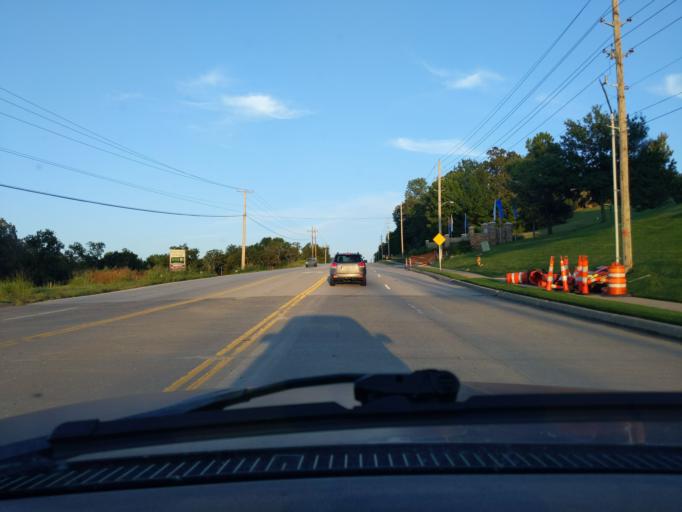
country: US
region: Oklahoma
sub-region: Tulsa County
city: Jenks
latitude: 36.0463
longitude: -95.9207
